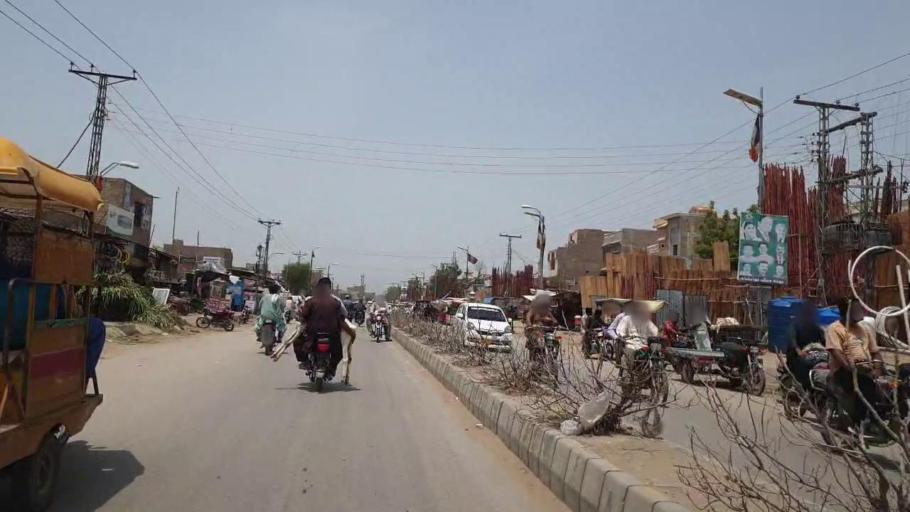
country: PK
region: Sindh
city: Nawabshah
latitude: 26.2521
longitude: 68.4169
